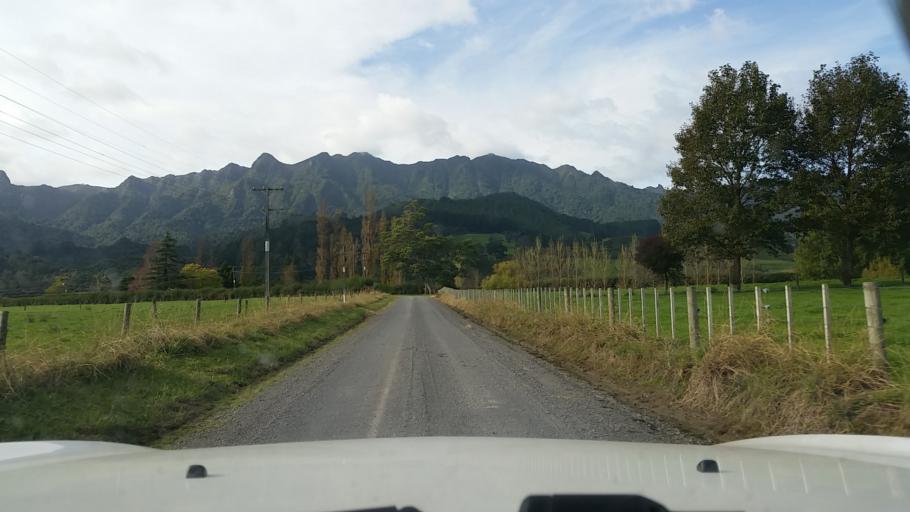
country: NZ
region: Bay of Plenty
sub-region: Western Bay of Plenty District
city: Katikati
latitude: -37.5760
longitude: 175.7601
